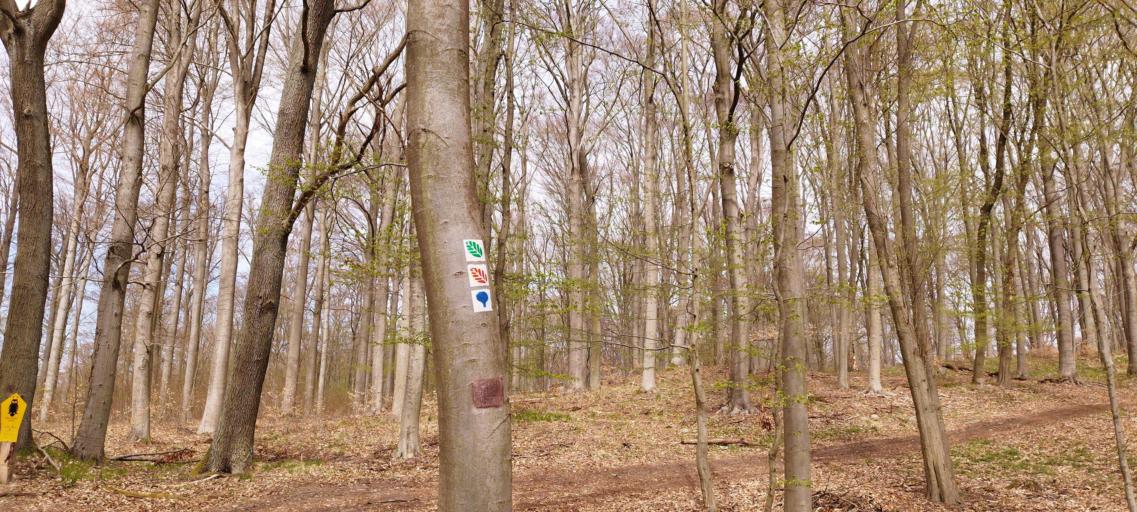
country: DE
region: Brandenburg
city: Althuttendorf
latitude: 52.9750
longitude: 13.8715
